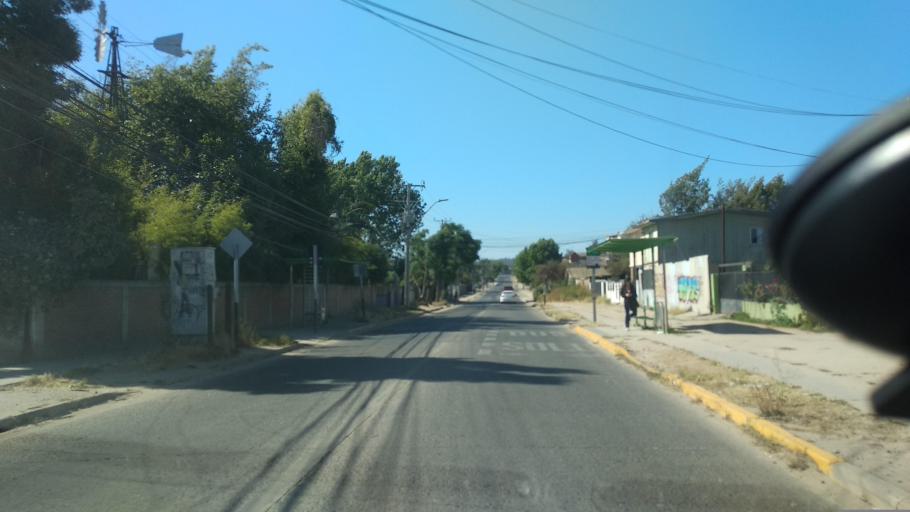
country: CL
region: Valparaiso
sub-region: Provincia de Marga Marga
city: Villa Alemana
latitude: -33.0542
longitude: -71.3738
